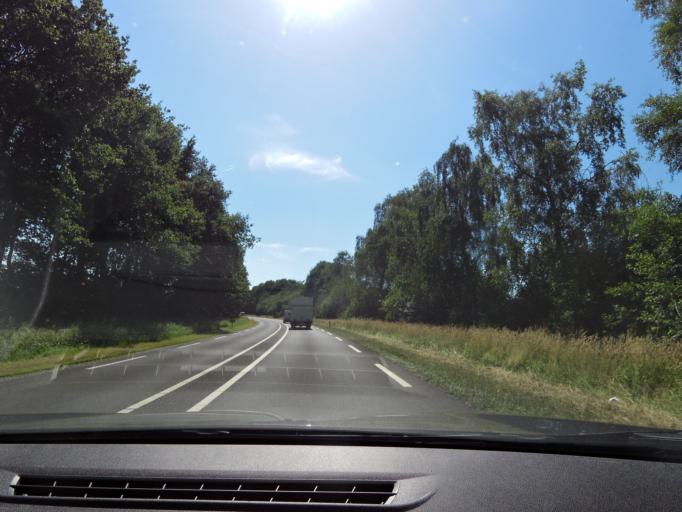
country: NL
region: Gelderland
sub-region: Oost Gelre
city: Lichtenvoorde
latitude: 52.0315
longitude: 6.6166
